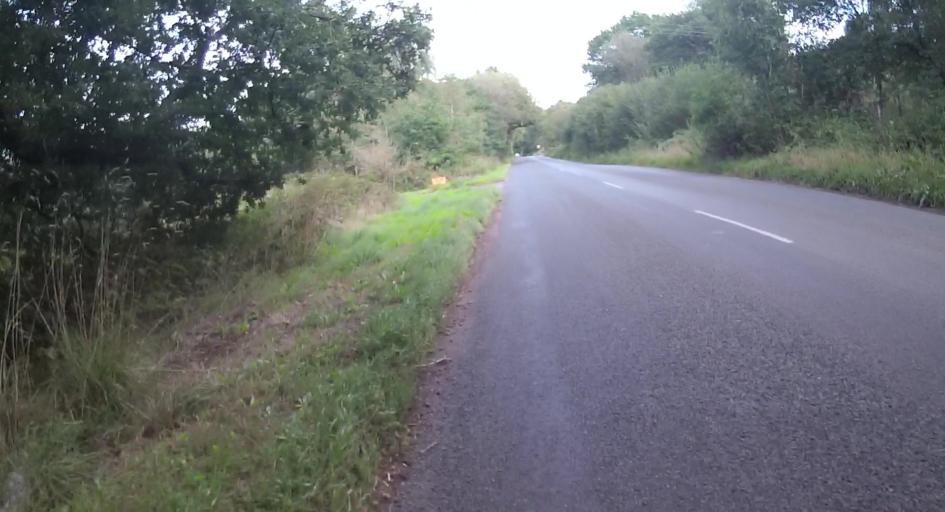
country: GB
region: England
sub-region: West Berkshire
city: Thatcham
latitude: 51.3766
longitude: -1.2390
